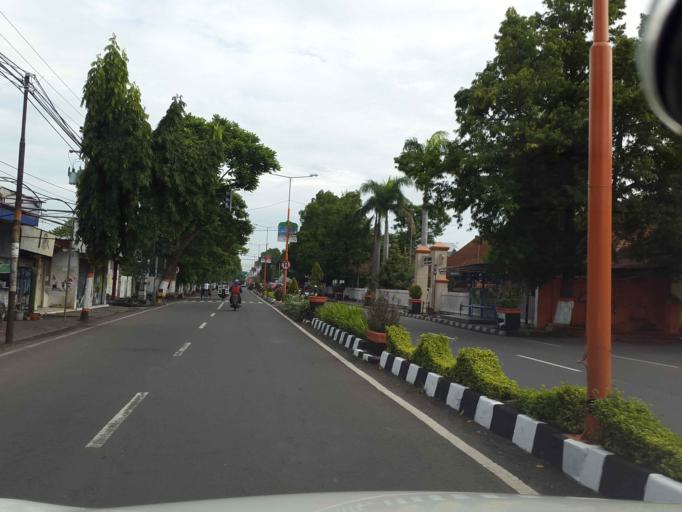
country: ID
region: East Java
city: Mojokerto
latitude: -7.4700
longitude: 112.4396
